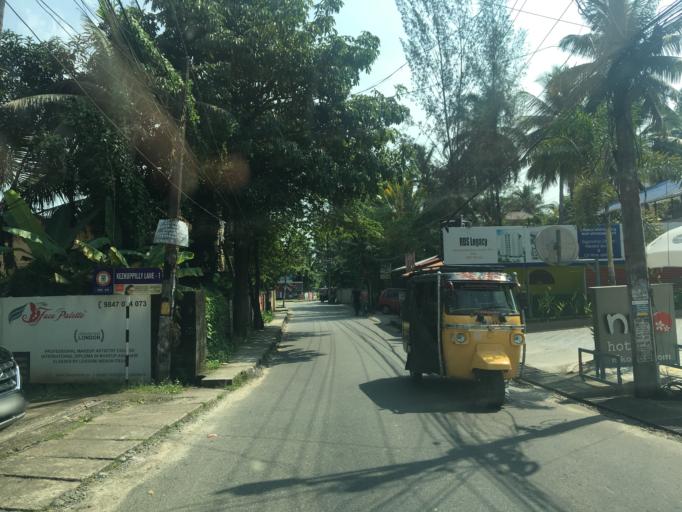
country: IN
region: Kerala
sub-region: Ernakulam
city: Cochin
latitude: 9.9581
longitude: 76.3021
